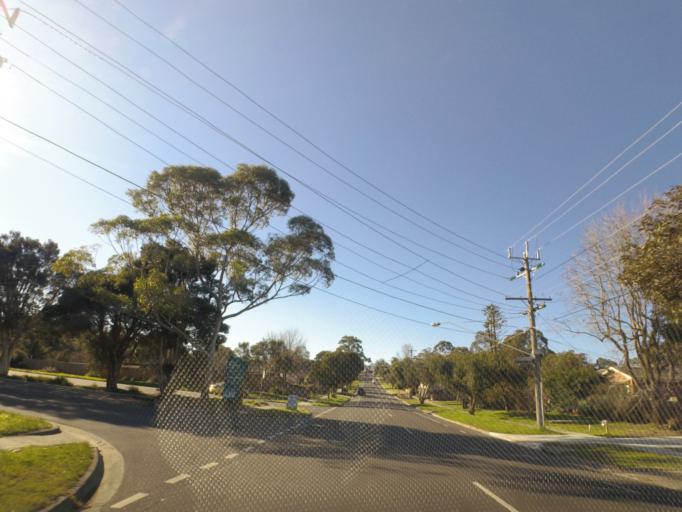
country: AU
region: Victoria
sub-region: Yarra Ranges
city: Kilsyth
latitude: -37.7953
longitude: 145.3136
